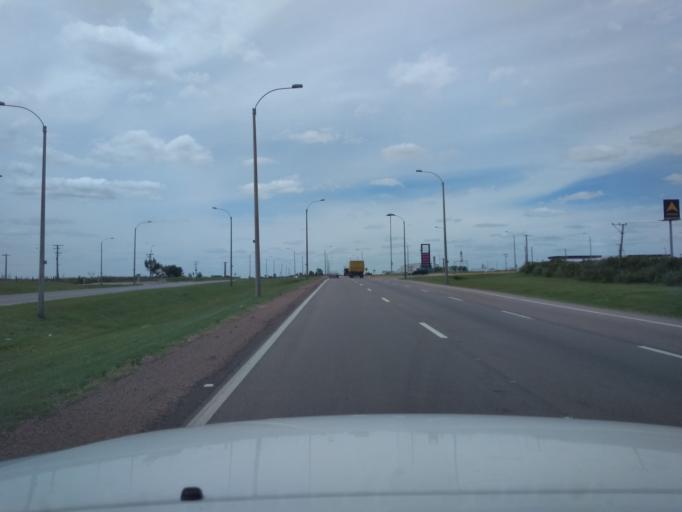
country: UY
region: Canelones
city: La Paz
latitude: -34.7517
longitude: -56.2561
